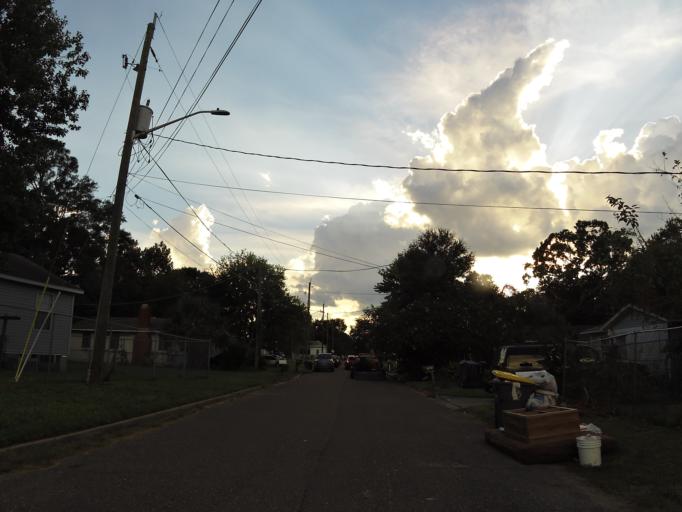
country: US
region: Florida
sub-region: Duval County
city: Jacksonville
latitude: 30.3388
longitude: -81.6785
